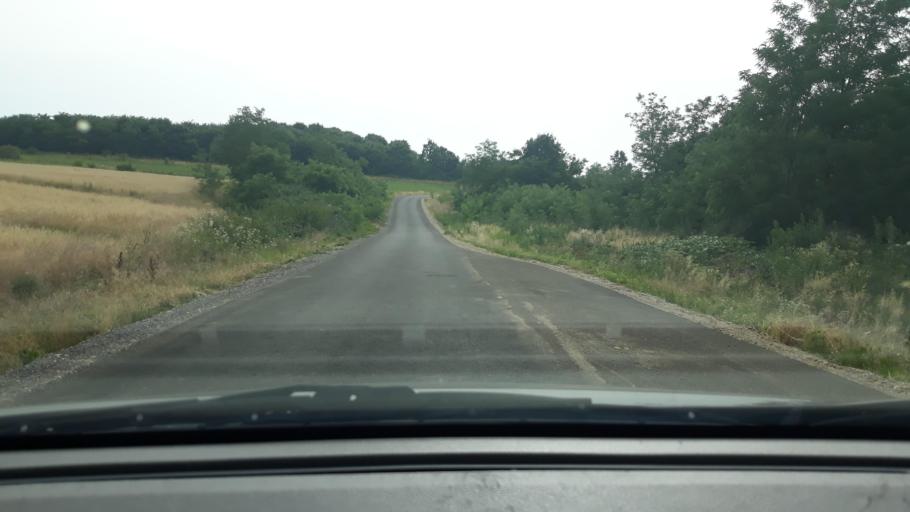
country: RO
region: Bihor
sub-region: Comuna Chislaz
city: Misca
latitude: 47.2618
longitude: 22.2963
